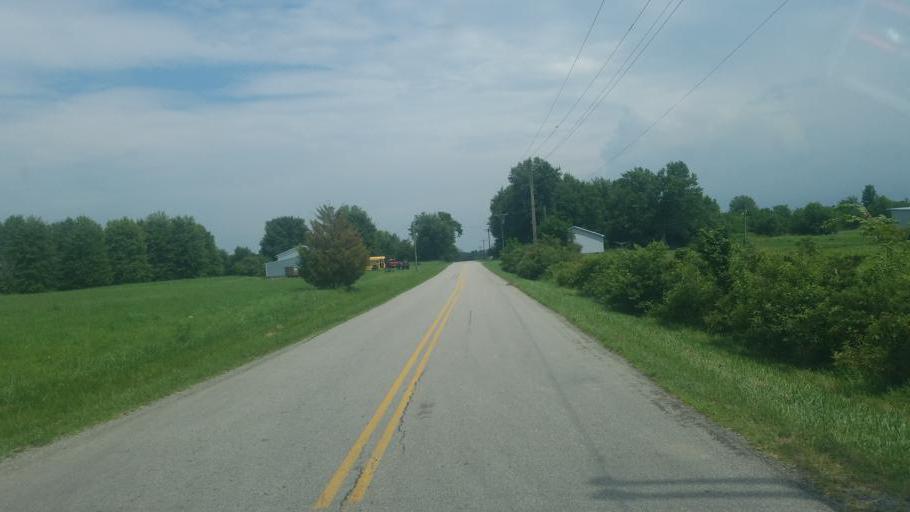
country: US
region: Ohio
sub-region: Union County
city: Richwood
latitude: 40.3904
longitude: -83.4750
